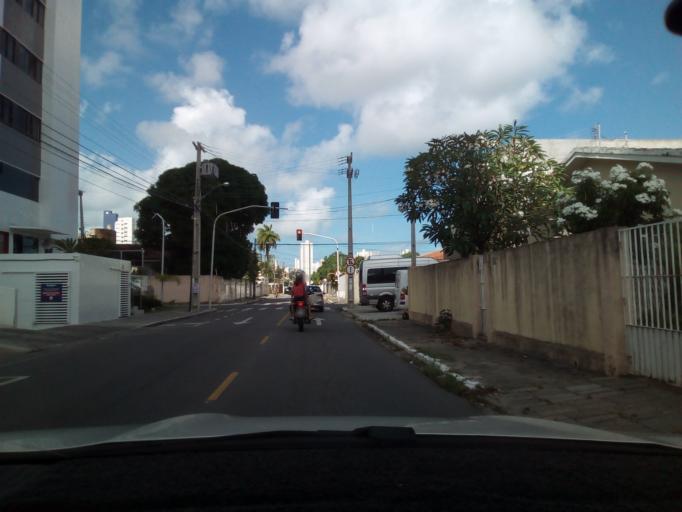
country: BR
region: Paraiba
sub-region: Joao Pessoa
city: Joao Pessoa
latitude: -7.1156
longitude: -34.8538
